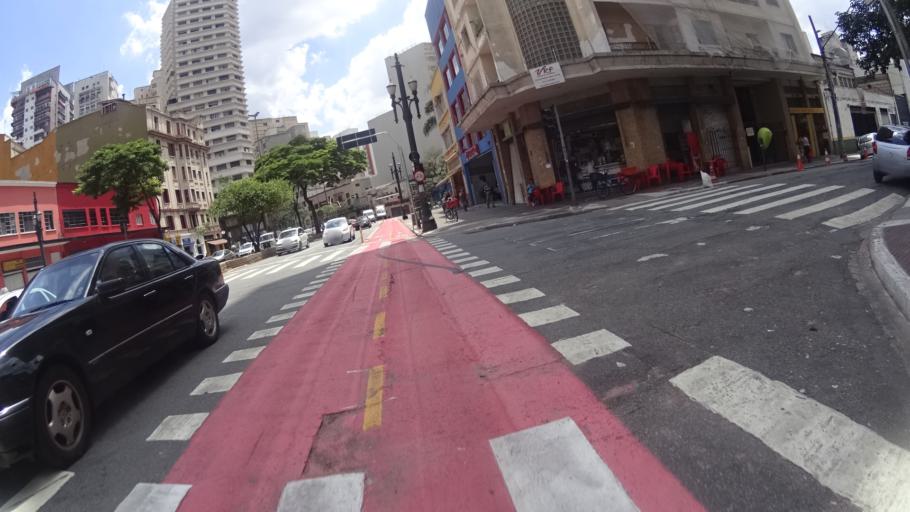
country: BR
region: Sao Paulo
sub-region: Sao Paulo
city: Sao Paulo
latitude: -23.5385
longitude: -46.6454
